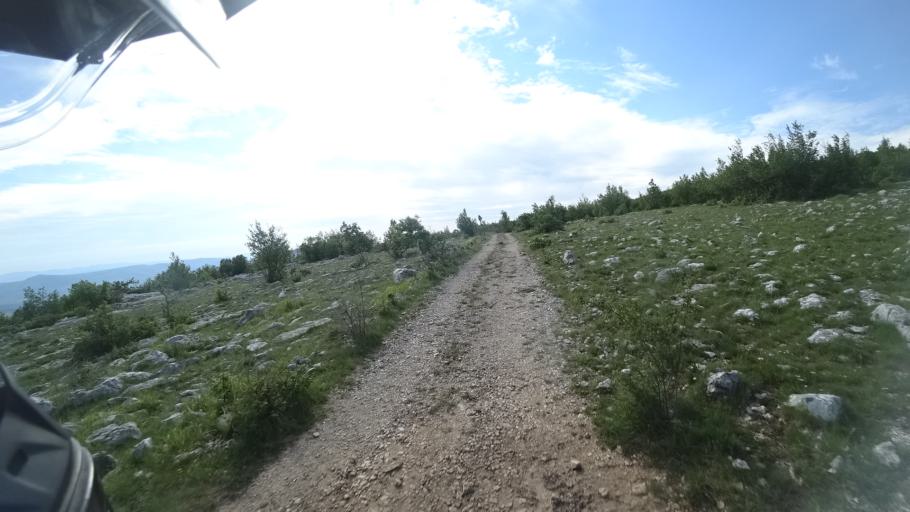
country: HR
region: Splitsko-Dalmatinska
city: Hrvace
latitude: 43.7817
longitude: 16.4408
